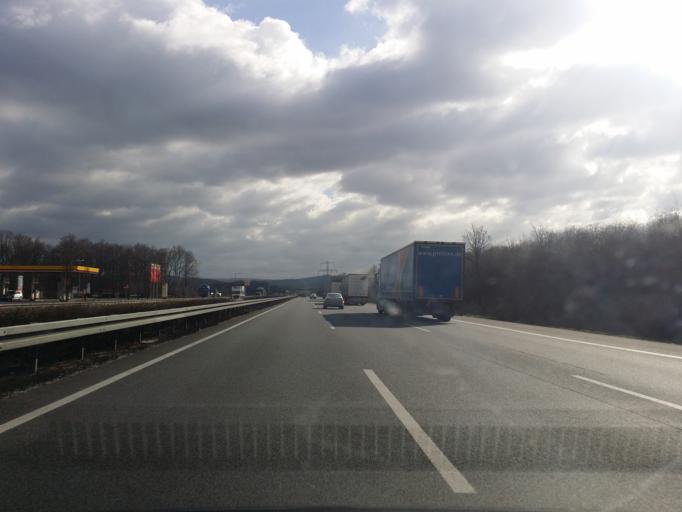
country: DE
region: Lower Saxony
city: Rosdorf
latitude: 51.4886
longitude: 9.8760
